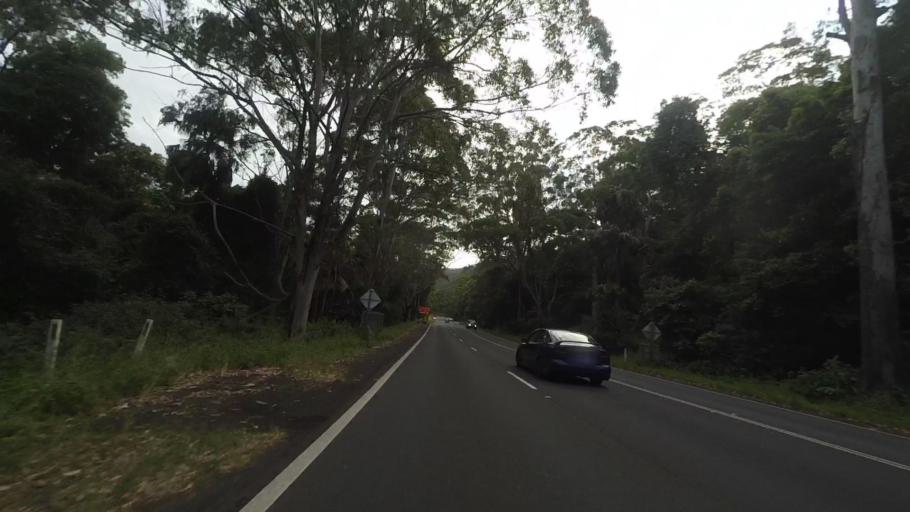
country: AU
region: New South Wales
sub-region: Wollongong
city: Bulli
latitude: -34.3192
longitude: 150.8969
